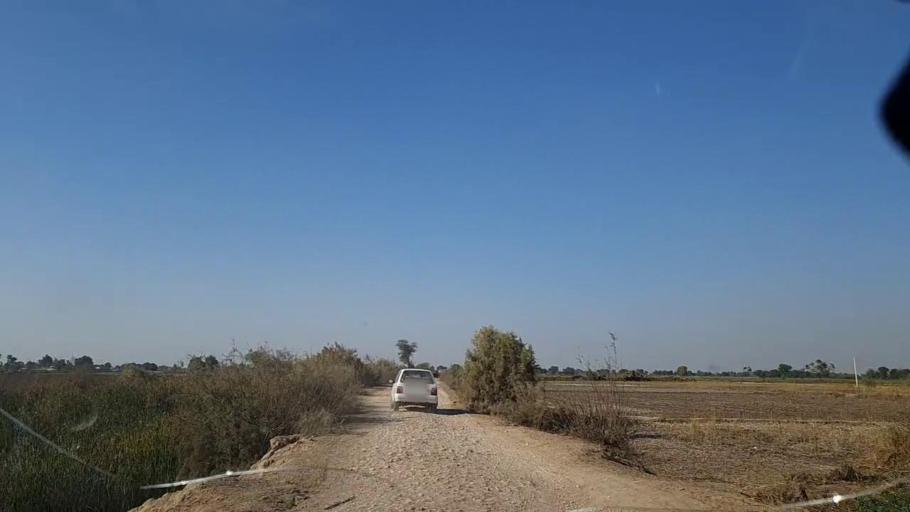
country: PK
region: Sindh
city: Khanpur
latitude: 27.7818
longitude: 69.3553
